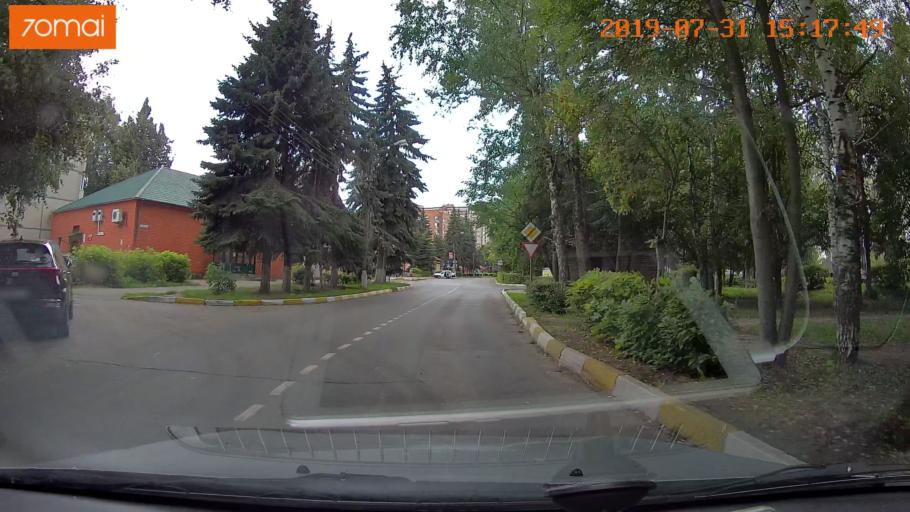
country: RU
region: Moskovskaya
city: Voskresensk
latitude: 55.3185
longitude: 38.6510
